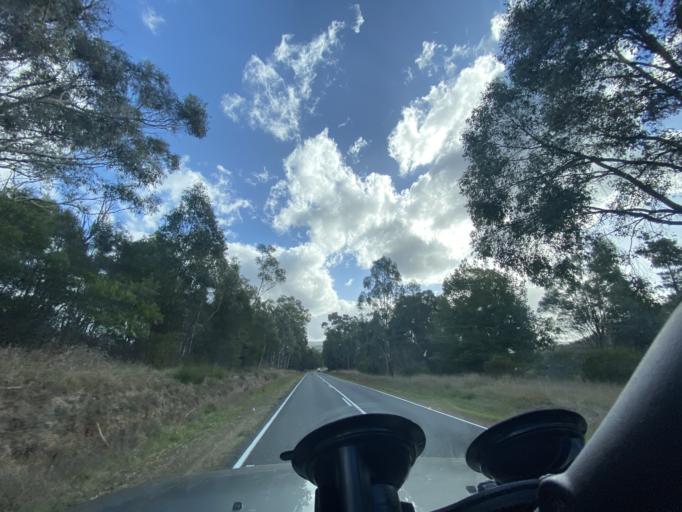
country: AU
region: Victoria
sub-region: Murrindindi
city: Kinglake West
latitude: -37.3224
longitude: 145.3105
